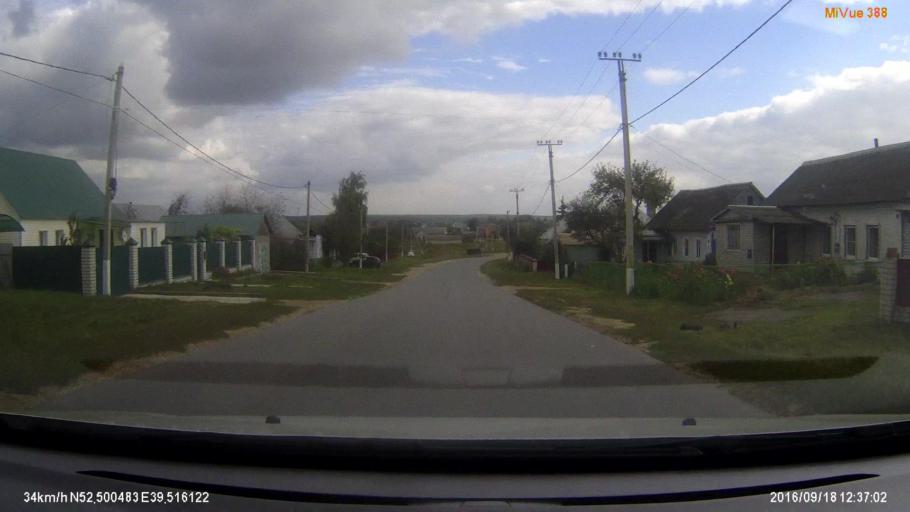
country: RU
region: Lipetsk
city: Syrskoye
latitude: 52.5003
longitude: 39.5167
